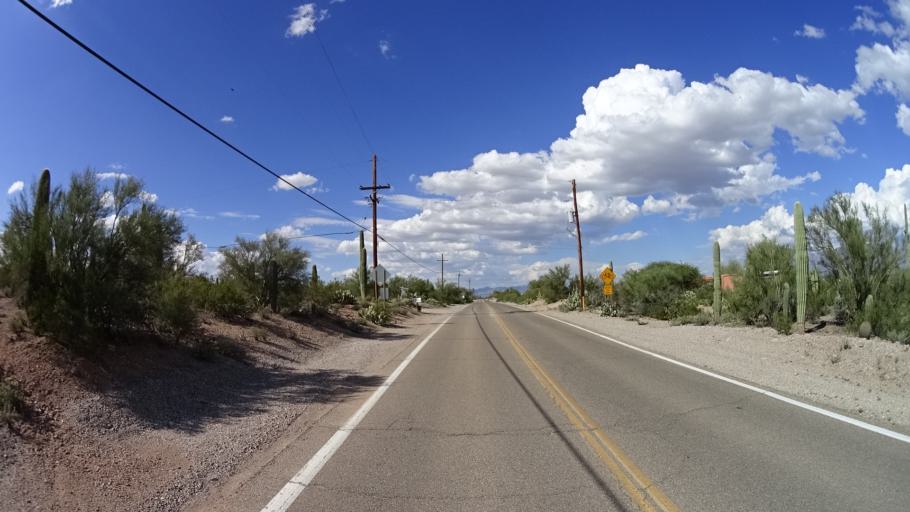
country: US
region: Arizona
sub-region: Pima County
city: Flowing Wells
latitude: 32.2600
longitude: -111.0628
